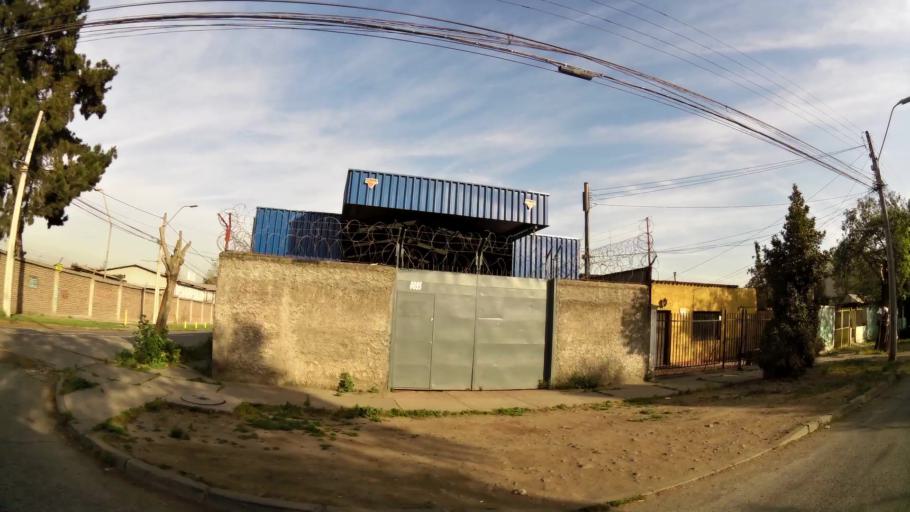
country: CL
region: Santiago Metropolitan
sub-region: Provincia de Santiago
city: La Pintana
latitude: -33.5242
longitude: -70.6746
